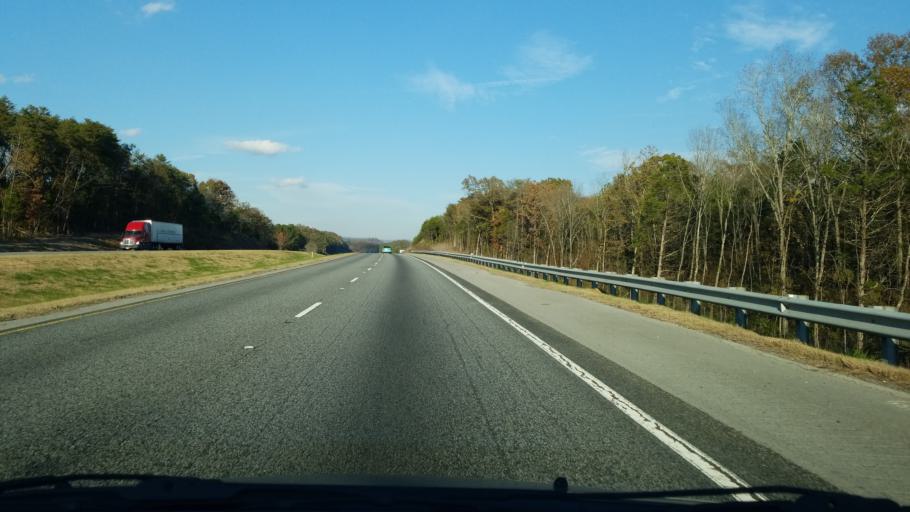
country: US
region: Georgia
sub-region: Dade County
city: Trenton
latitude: 34.8911
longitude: -85.5014
